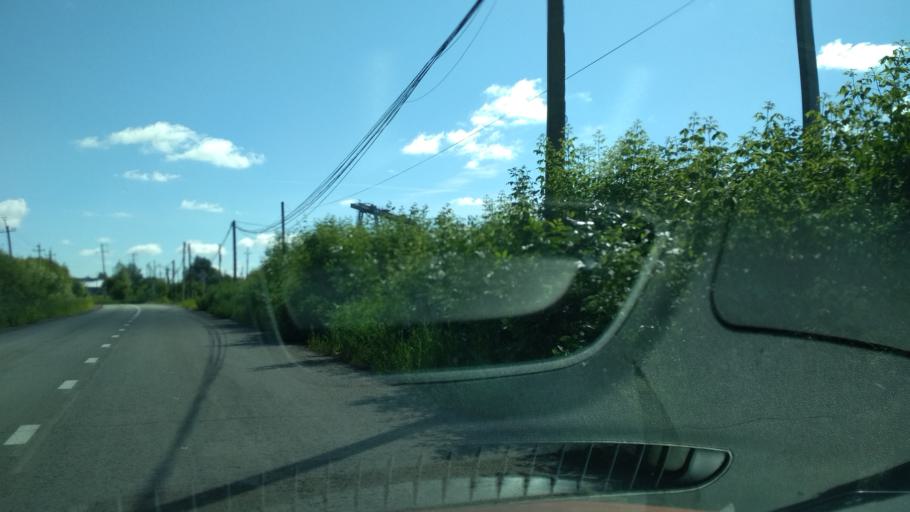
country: RU
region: Tatarstan
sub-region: Tukayevskiy Rayon
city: Naberezhnyye Chelny
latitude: 55.6530
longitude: 52.2993
